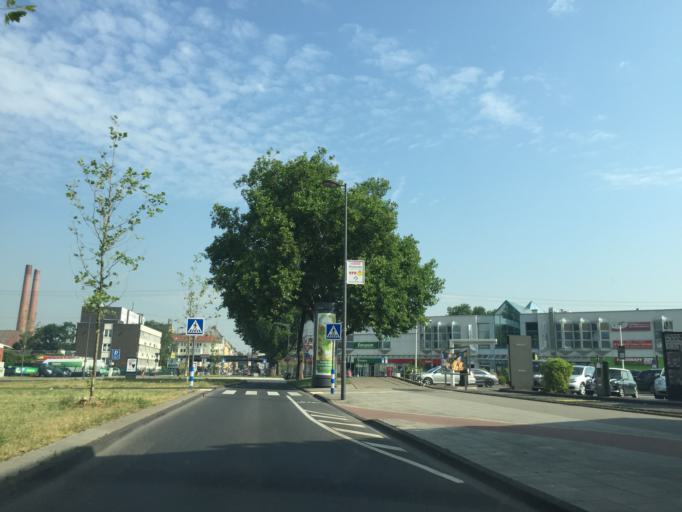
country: DE
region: North Rhine-Westphalia
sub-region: Regierungsbezirk Koln
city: Bayenthal
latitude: 50.9138
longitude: 6.9619
